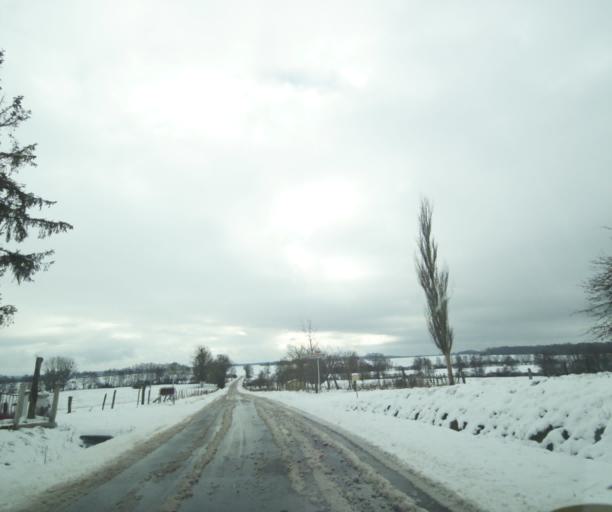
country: FR
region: Champagne-Ardenne
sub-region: Departement de la Haute-Marne
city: Montier-en-Der
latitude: 48.4541
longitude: 4.6943
